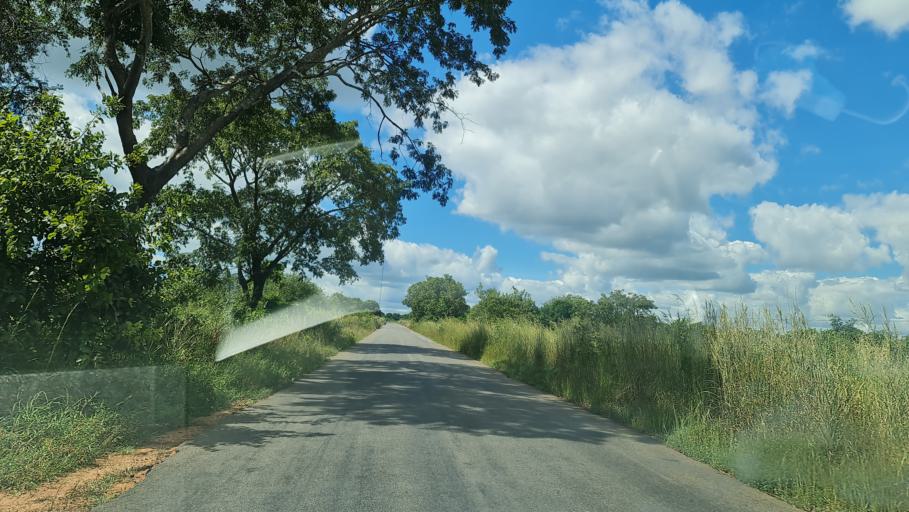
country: MZ
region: Zambezia
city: Quelimane
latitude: -17.5082
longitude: 36.2381
